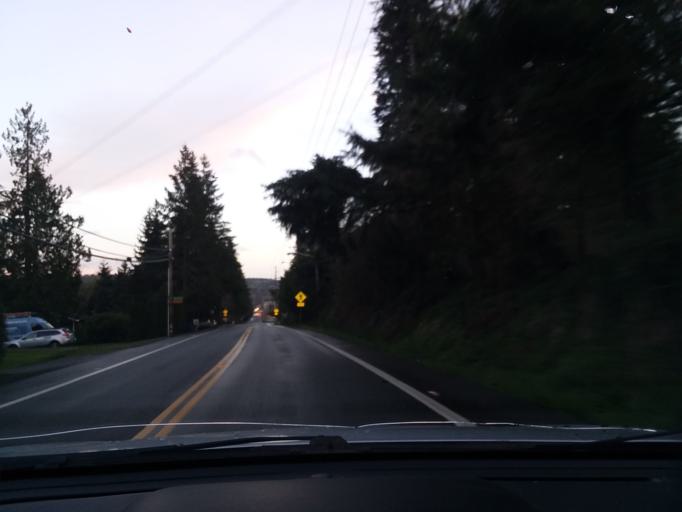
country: US
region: Washington
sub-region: King County
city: Kenmore
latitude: 47.7675
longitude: -122.2495
